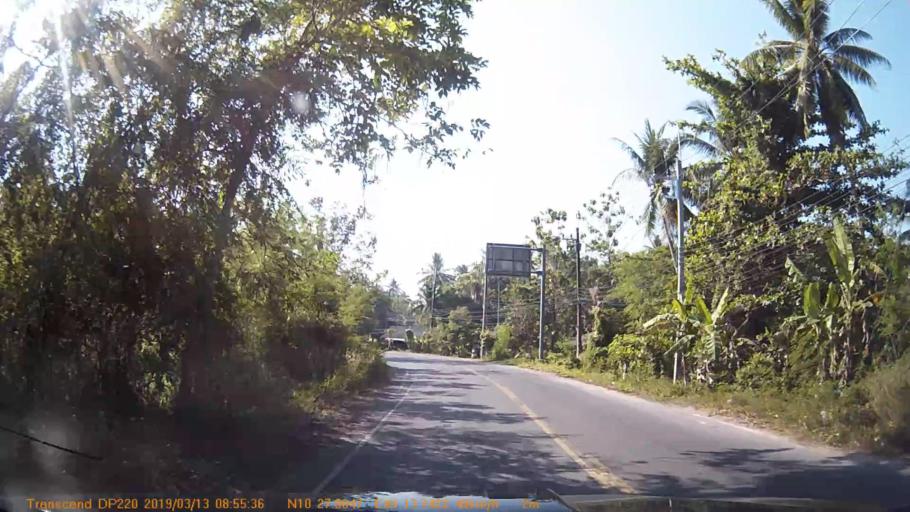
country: TH
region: Chumphon
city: Chumphon
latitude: 10.4649
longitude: 99.2291
